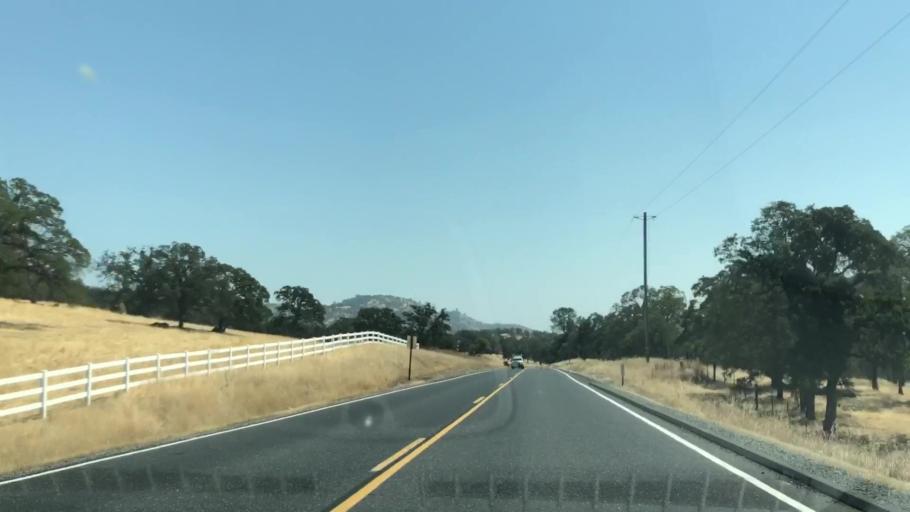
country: US
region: California
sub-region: Calaveras County
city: Copperopolis
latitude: 37.9724
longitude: -120.6300
